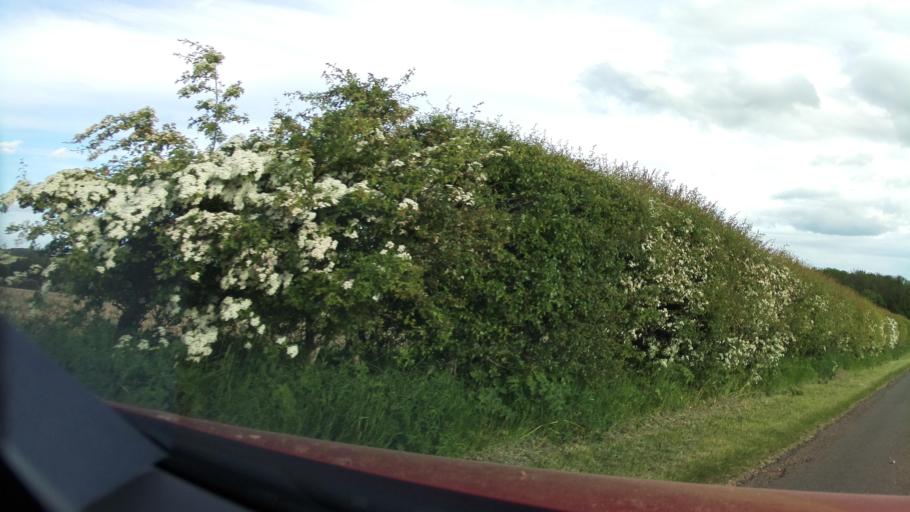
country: GB
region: England
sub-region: Gloucestershire
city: Westfield
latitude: 51.8873
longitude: -1.8885
